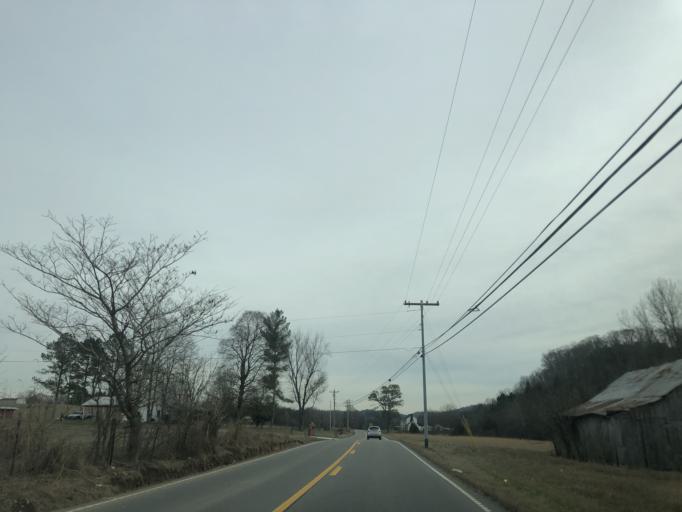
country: US
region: Tennessee
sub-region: Sumner County
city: White House
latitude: 36.4651
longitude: -86.5594
